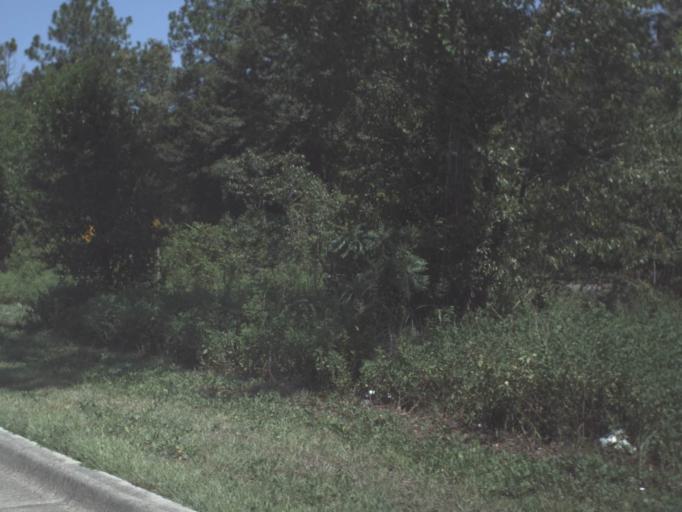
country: US
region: Florida
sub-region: Taylor County
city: Perry
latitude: 30.0906
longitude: -83.5359
